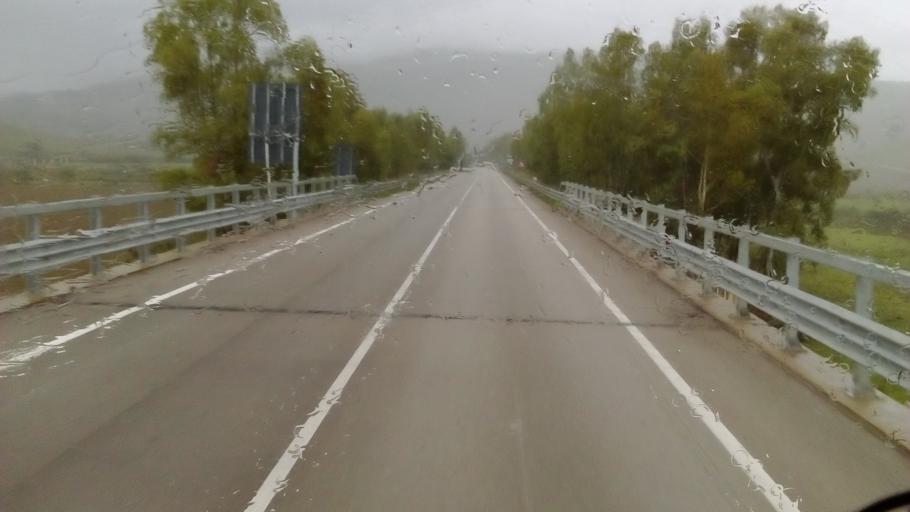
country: IT
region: Sicily
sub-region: Enna
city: Villarosa
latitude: 37.5297
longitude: 14.1292
